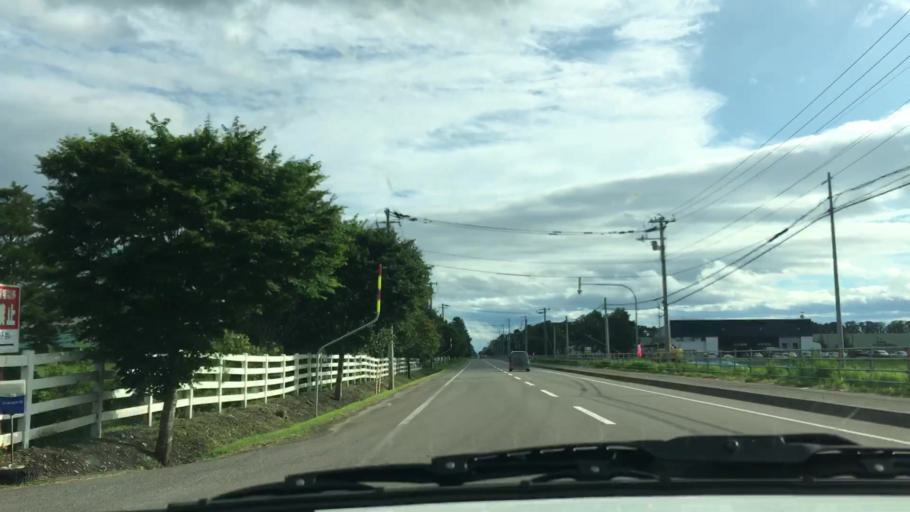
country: JP
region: Hokkaido
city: Otofuke
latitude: 43.2524
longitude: 143.2995
